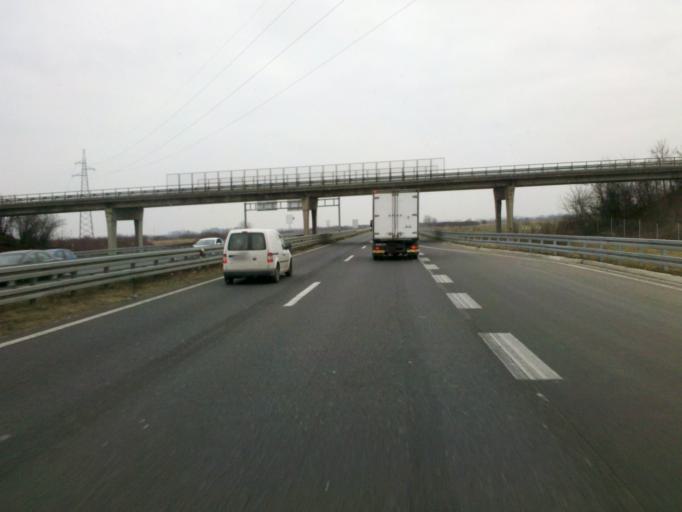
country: HR
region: Grad Zagreb
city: Odra
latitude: 45.7504
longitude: 16.0117
